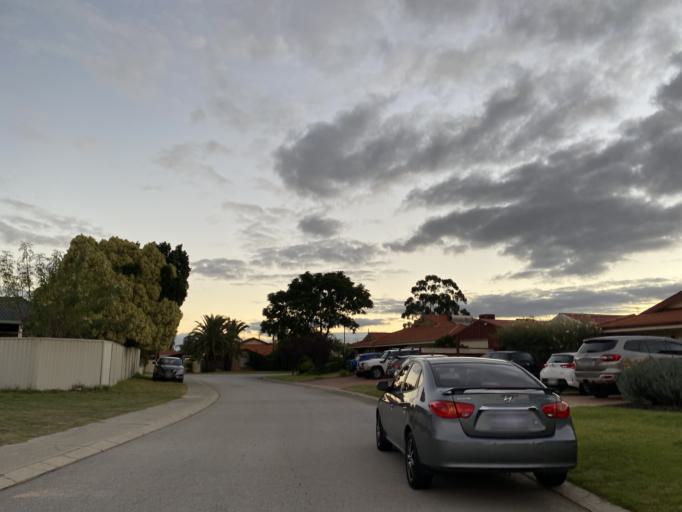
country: AU
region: Western Australia
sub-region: Belmont
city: Kewdale
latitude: -31.9890
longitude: 115.9917
